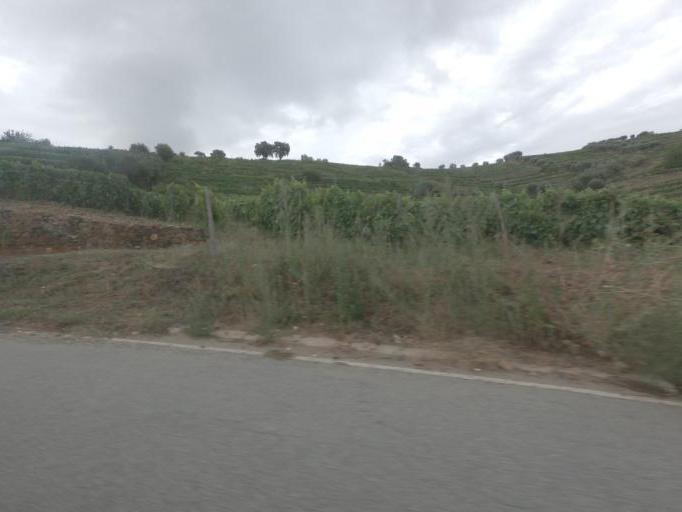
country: PT
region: Vila Real
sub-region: Sabrosa
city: Sabrosa
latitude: 41.2796
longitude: -7.5508
